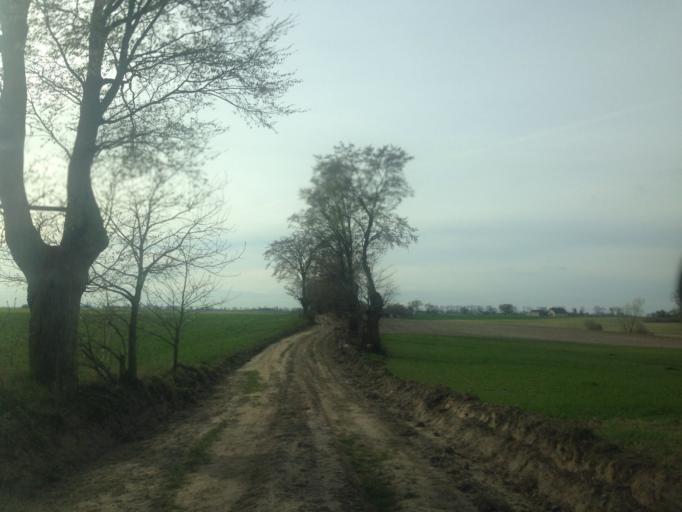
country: PL
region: Kujawsko-Pomorskie
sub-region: Powiat brodnicki
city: Jablonowo Pomorskie
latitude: 53.3746
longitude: 19.2433
